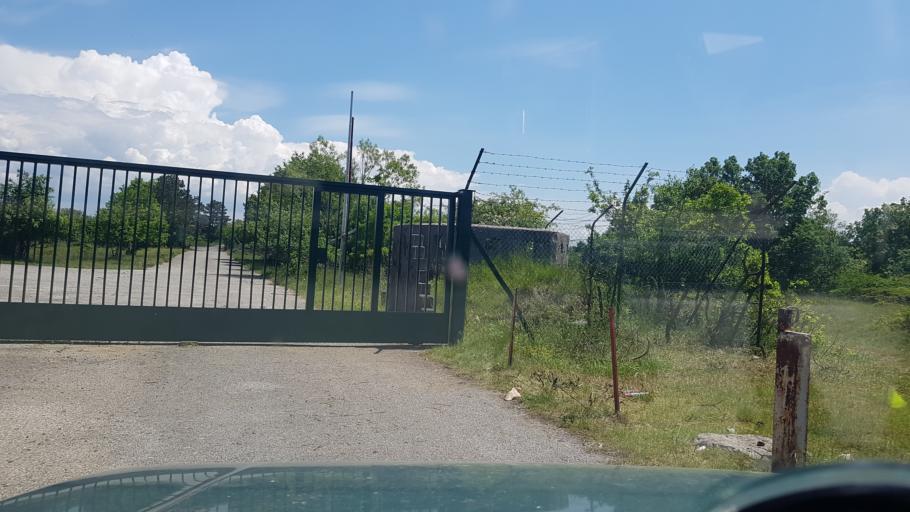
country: IT
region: Friuli Venezia Giulia
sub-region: Provincia di Trieste
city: Villa Opicina
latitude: 45.7092
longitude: 13.7794
